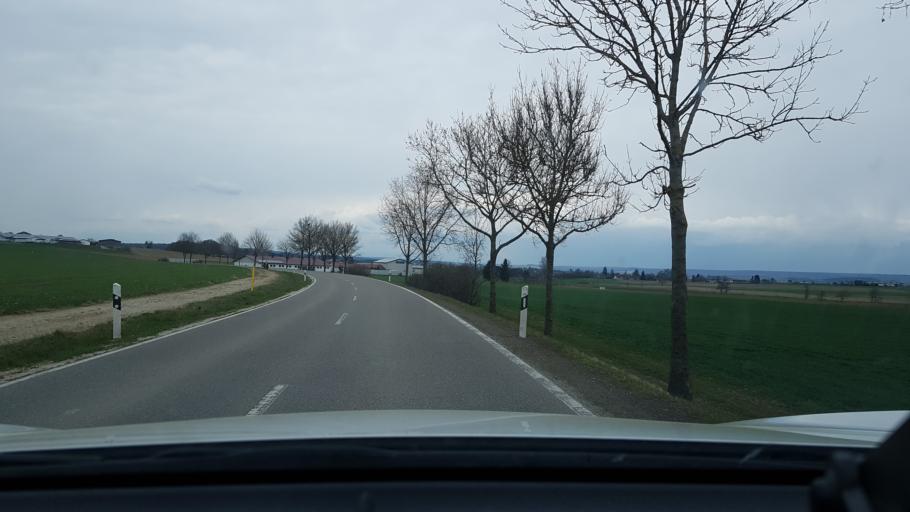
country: DE
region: Baden-Wuerttemberg
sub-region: Tuebingen Region
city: Oberstadion
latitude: 48.1817
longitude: 9.7186
